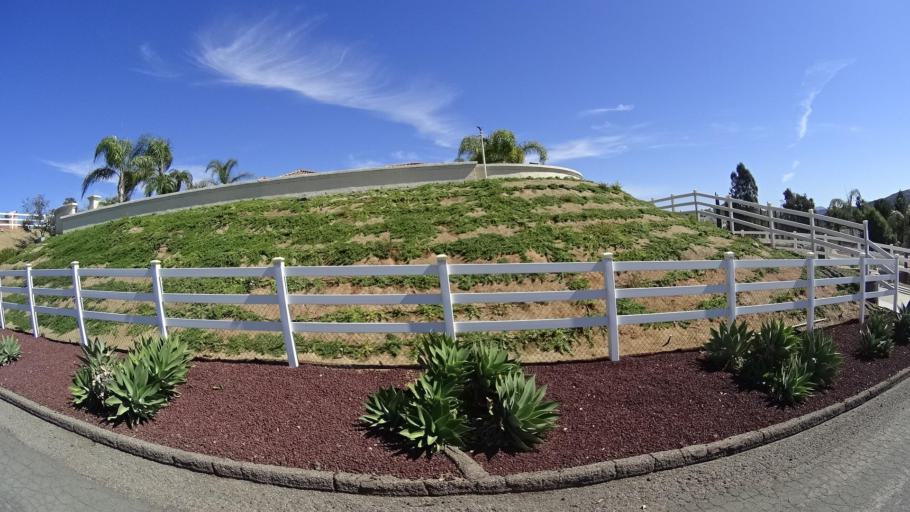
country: US
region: California
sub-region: San Diego County
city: Harbison Canyon
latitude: 32.8718
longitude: -116.8382
